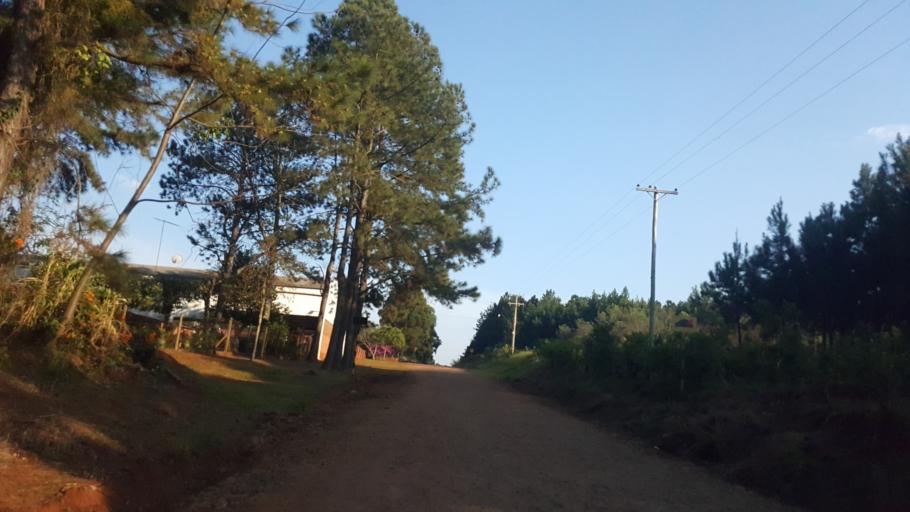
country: AR
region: Misiones
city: Capiovi
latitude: -26.8885
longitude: -55.0604
